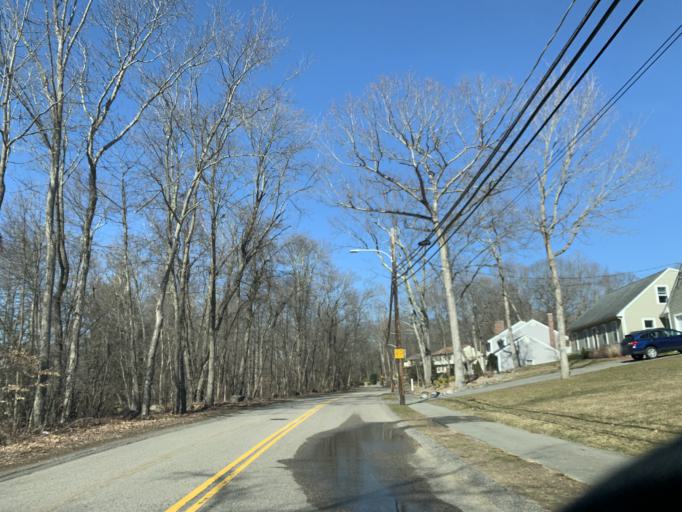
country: US
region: Massachusetts
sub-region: Norfolk County
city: Westwood
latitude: 42.1908
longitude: -71.2230
